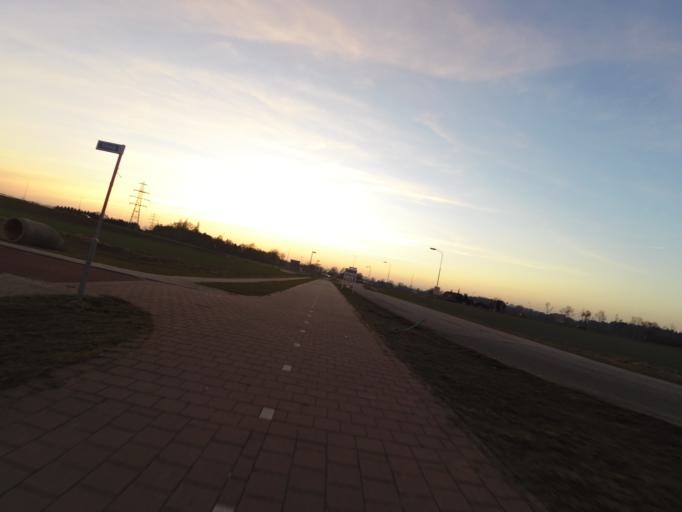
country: NL
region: Gelderland
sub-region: Gemeente Zevenaar
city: Zevenaar
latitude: 51.9209
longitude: 6.0933
